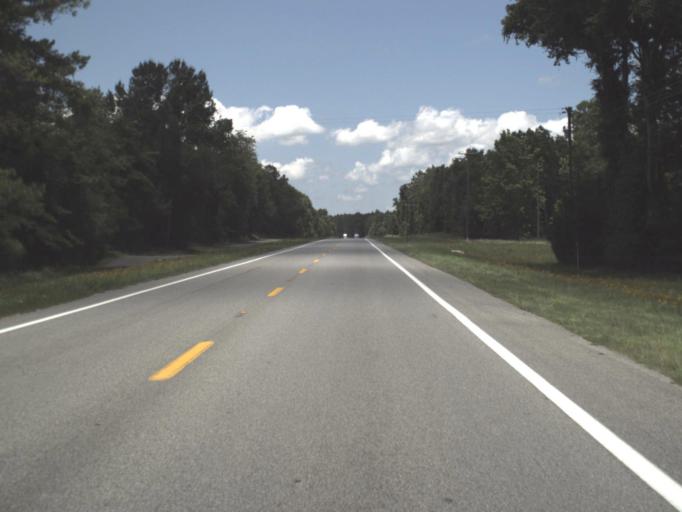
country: US
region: Florida
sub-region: Alachua County
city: High Springs
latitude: 29.9439
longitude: -82.7436
